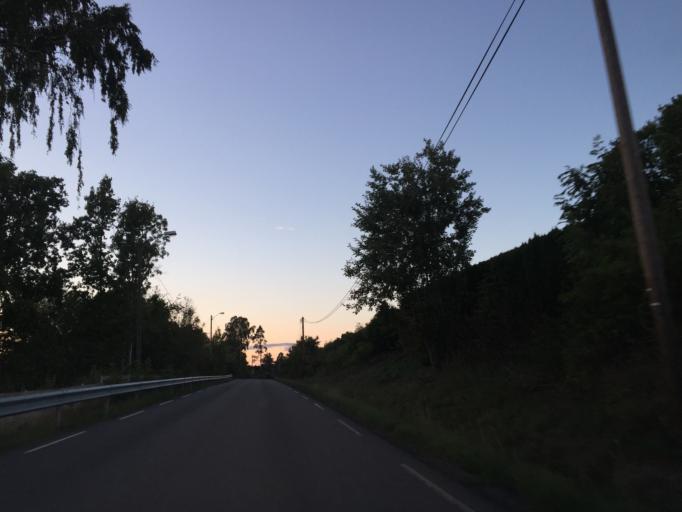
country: NO
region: Ostfold
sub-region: Moss
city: Moss
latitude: 59.5004
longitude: 10.6861
